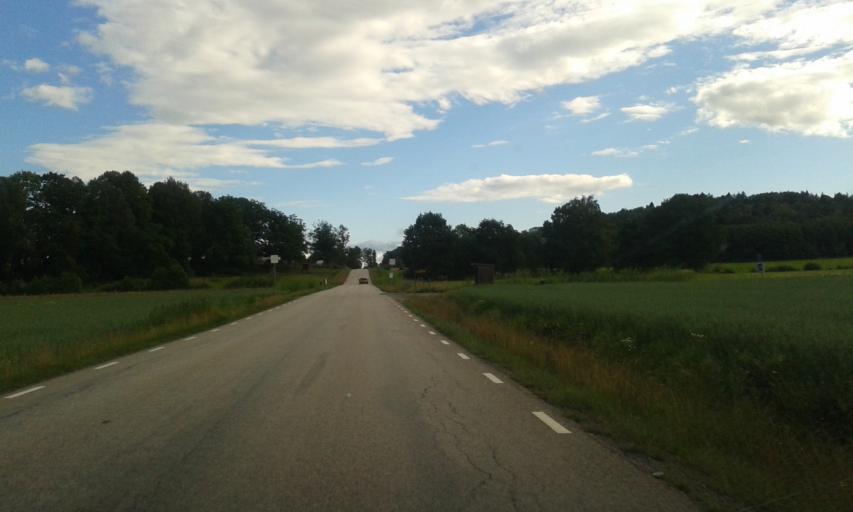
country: SE
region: Vaestra Goetaland
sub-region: Ale Kommun
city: Alvangen
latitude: 57.9761
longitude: 12.1095
